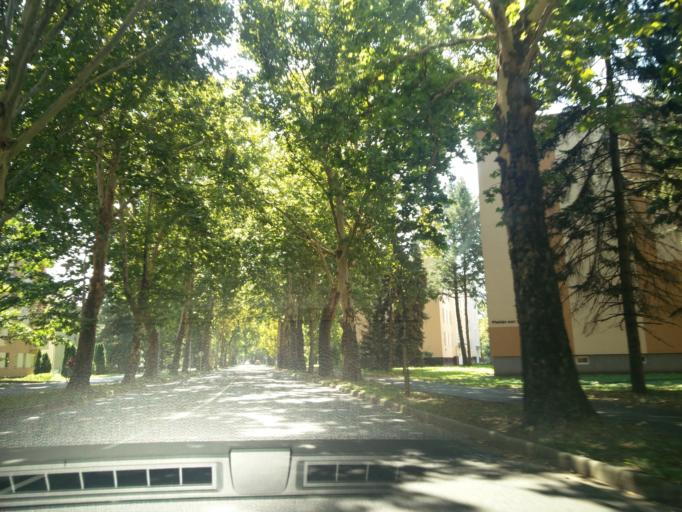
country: HU
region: Zala
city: Zalaegerszeg
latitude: 46.8433
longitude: 16.8313
